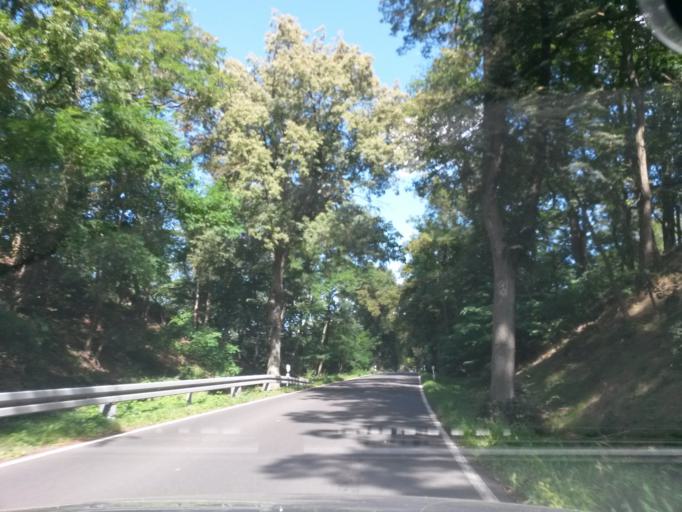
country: DE
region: Brandenburg
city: Schoneberg
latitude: 52.9869
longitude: 14.1033
